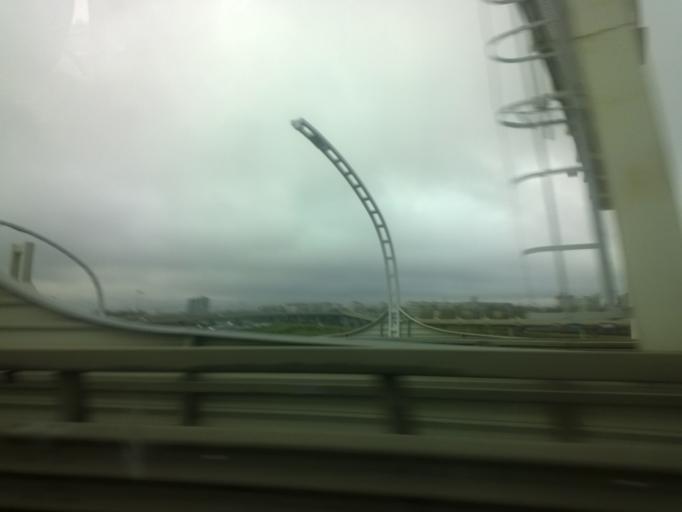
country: RU
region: St.-Petersburg
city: Dachnoye
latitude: 59.8352
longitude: 30.2797
